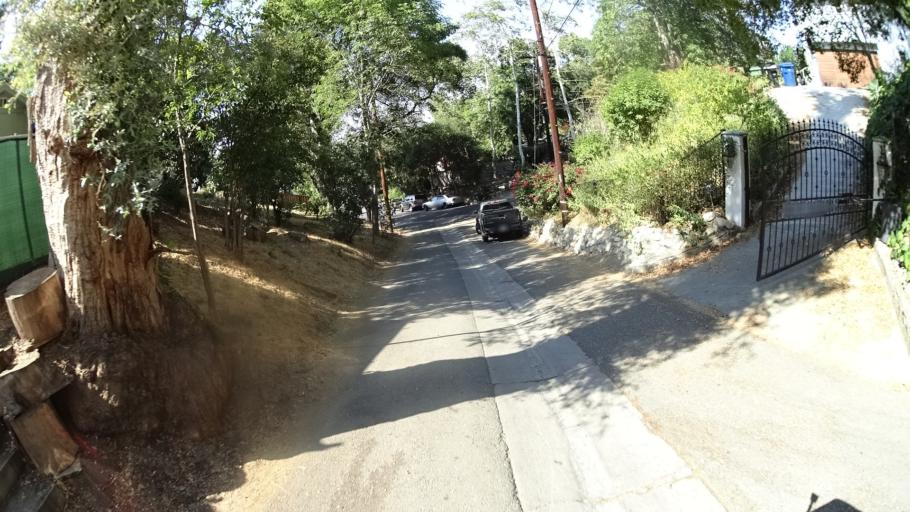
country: US
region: California
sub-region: Los Angeles County
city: Universal City
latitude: 34.1372
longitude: -118.3821
